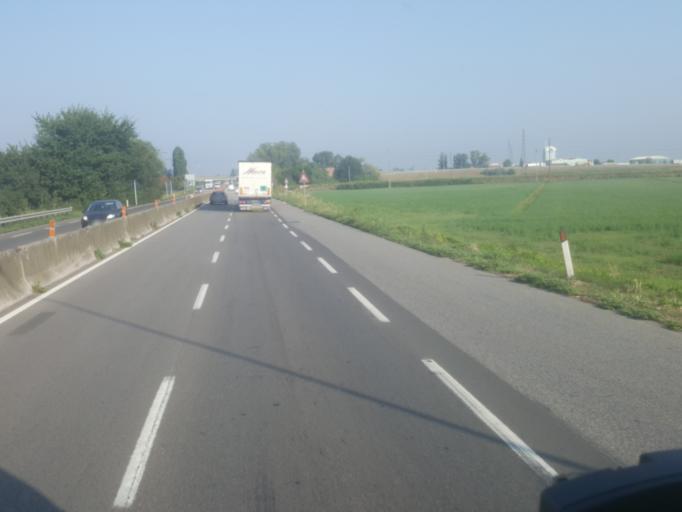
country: IT
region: Emilia-Romagna
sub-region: Provincia di Ravenna
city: Fornace Zarattini
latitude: 44.4244
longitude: 12.1597
